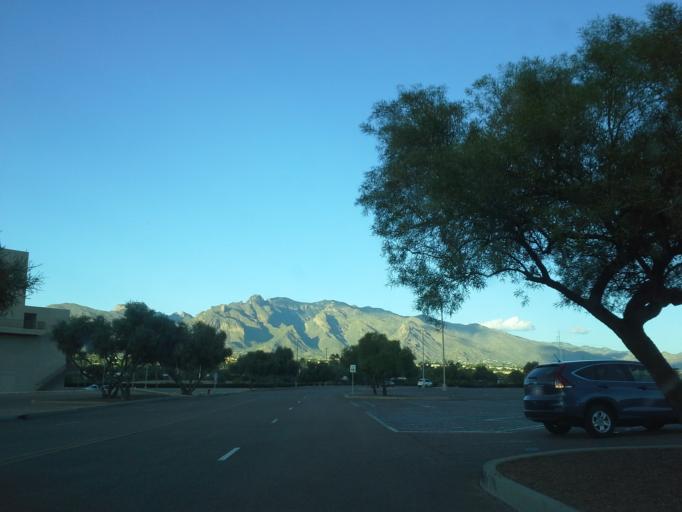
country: US
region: Arizona
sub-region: Pima County
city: Flowing Wells
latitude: 32.2906
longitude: -110.9767
